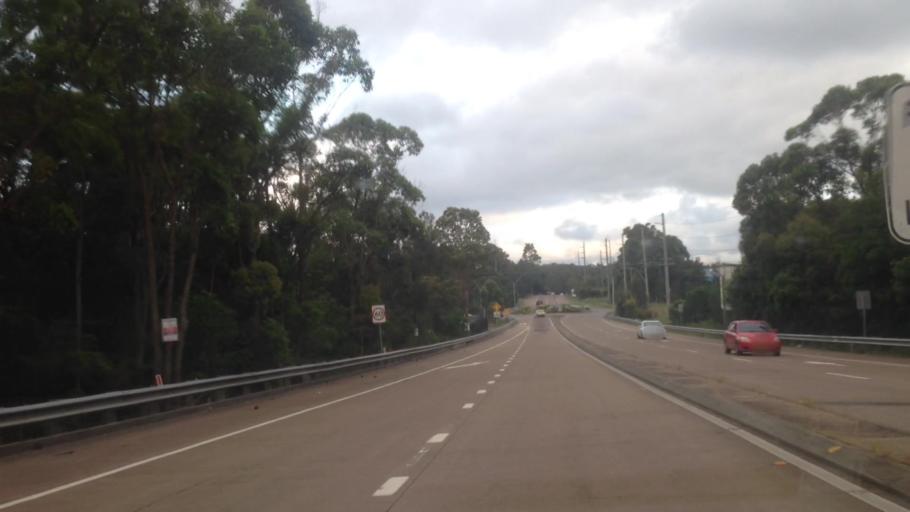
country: AU
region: New South Wales
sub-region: Lake Macquarie Shire
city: Cooranbong
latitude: -33.1172
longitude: 151.4680
